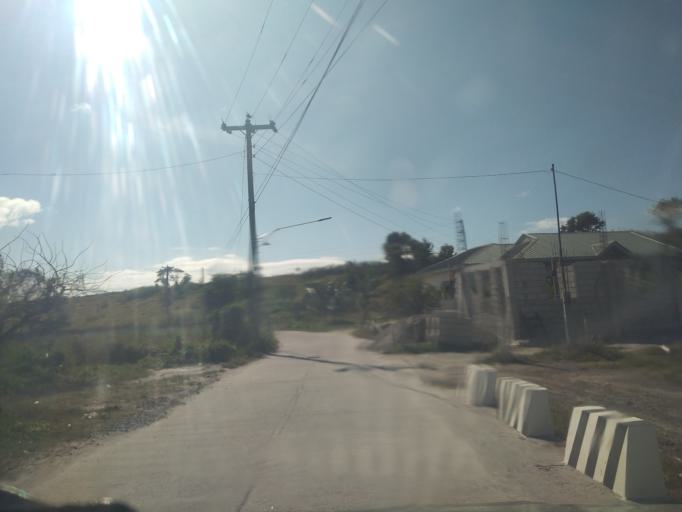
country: PH
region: Central Luzon
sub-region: Province of Pampanga
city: Calibutbut
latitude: 15.0930
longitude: 120.5931
